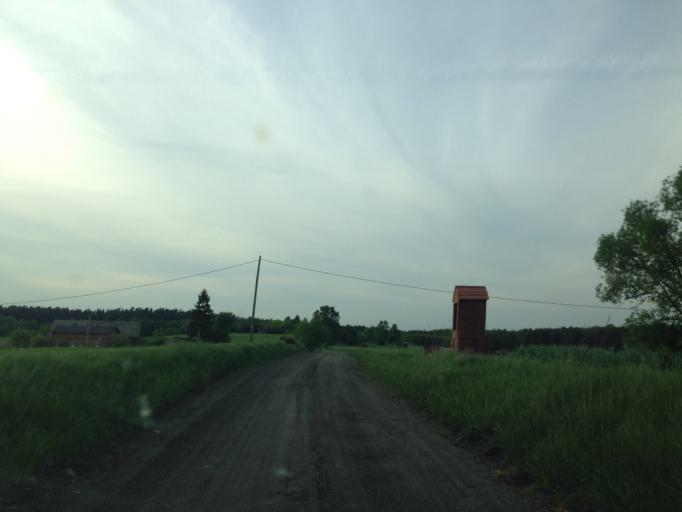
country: PL
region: Kujawsko-Pomorskie
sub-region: Powiat brodnicki
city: Brodnica
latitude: 53.3115
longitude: 19.3606
